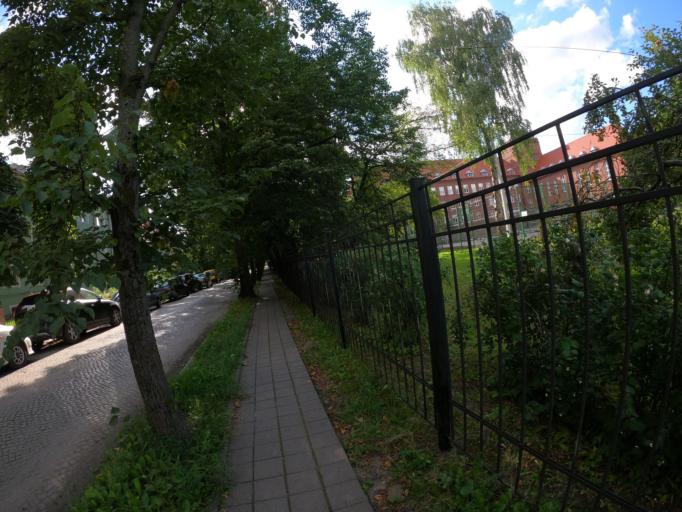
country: RU
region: Kaliningrad
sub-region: Gorod Kaliningrad
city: Kaliningrad
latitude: 54.7291
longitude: 20.4710
